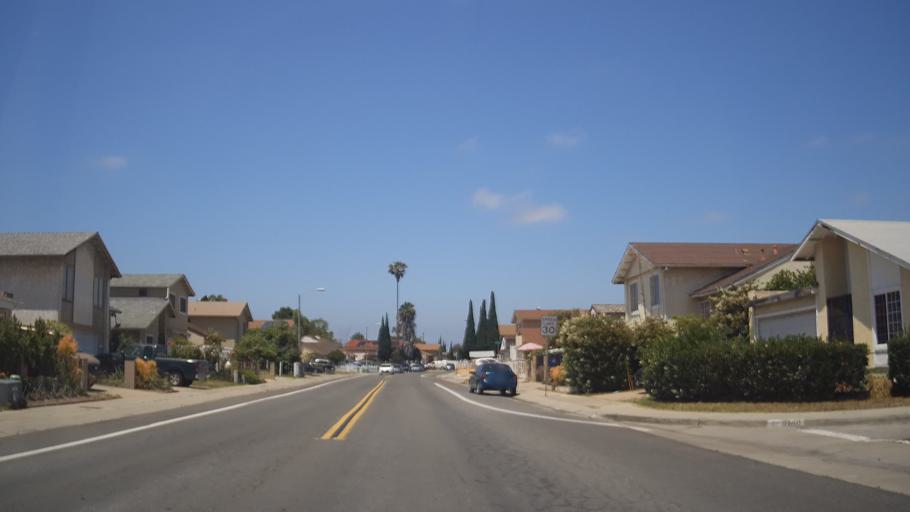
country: US
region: California
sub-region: San Diego County
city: Bonita
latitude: 32.6664
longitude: -117.0536
